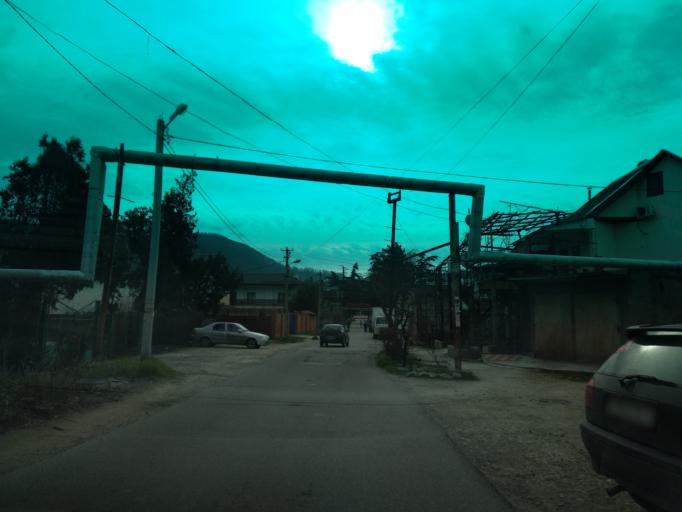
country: RU
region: Krasnodarskiy
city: Novomikhaylovskiy
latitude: 44.2516
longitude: 38.8422
